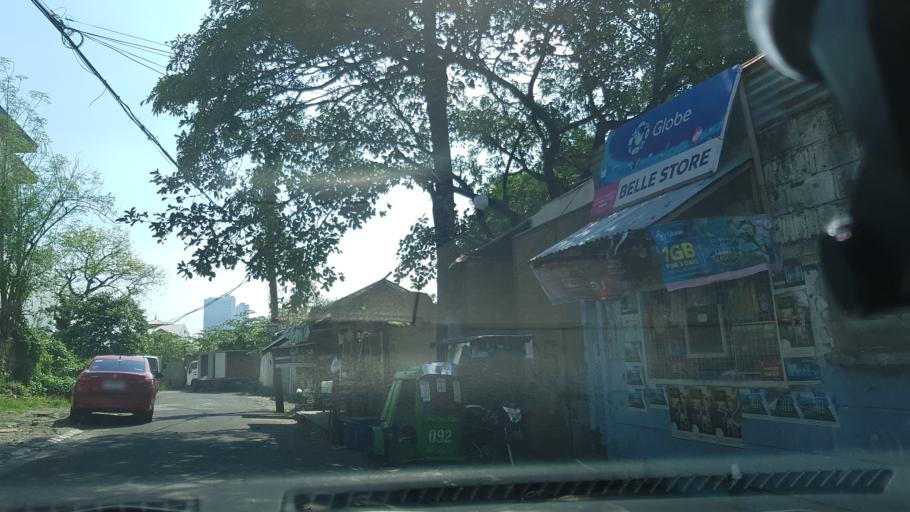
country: PH
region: Metro Manila
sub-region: San Juan
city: San Juan
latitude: 14.6160
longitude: 121.0294
